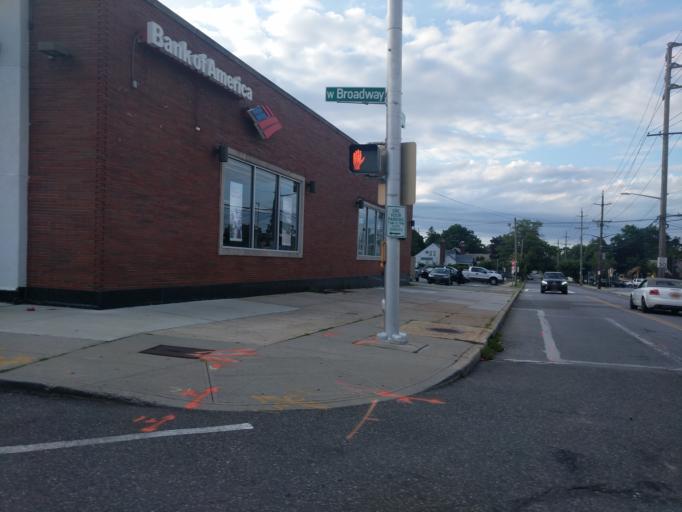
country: US
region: New York
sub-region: Nassau County
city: Hewlett
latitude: 40.6390
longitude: -73.7014
